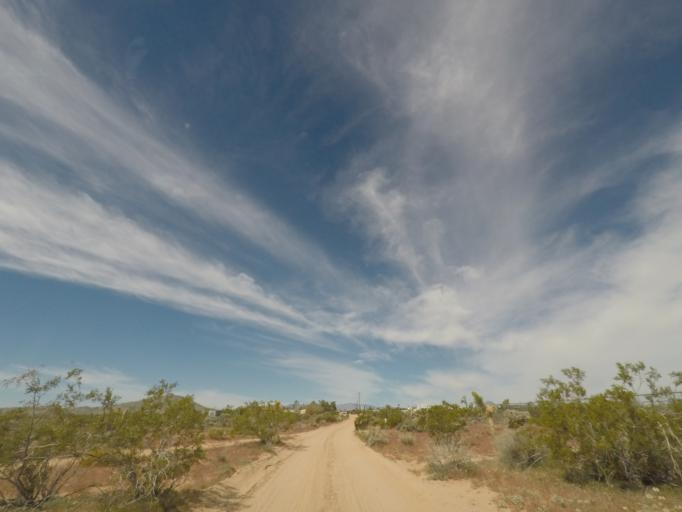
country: US
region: California
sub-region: San Bernardino County
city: Joshua Tree
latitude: 34.1953
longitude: -116.2851
